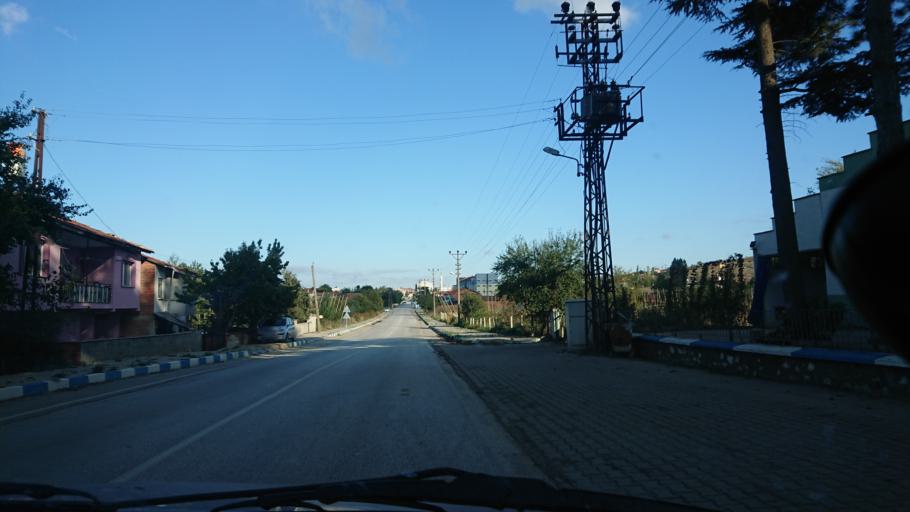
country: TR
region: Bilecik
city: Pazaryeri
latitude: 39.9993
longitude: 29.8891
